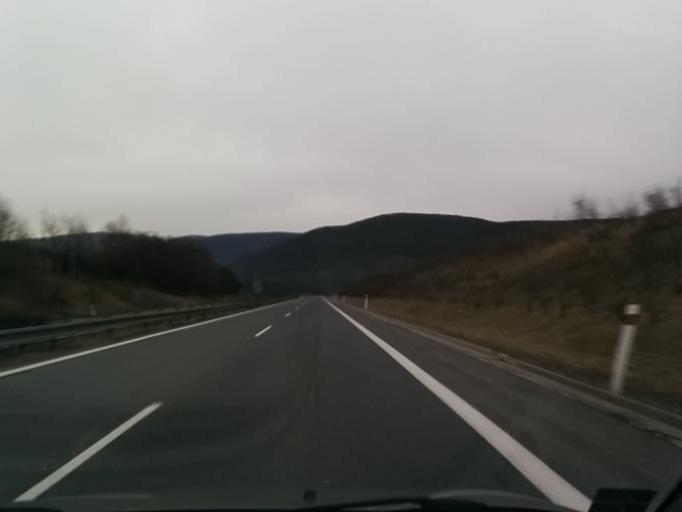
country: SK
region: Nitriansky
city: Tlmace
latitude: 48.3684
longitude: 18.5434
